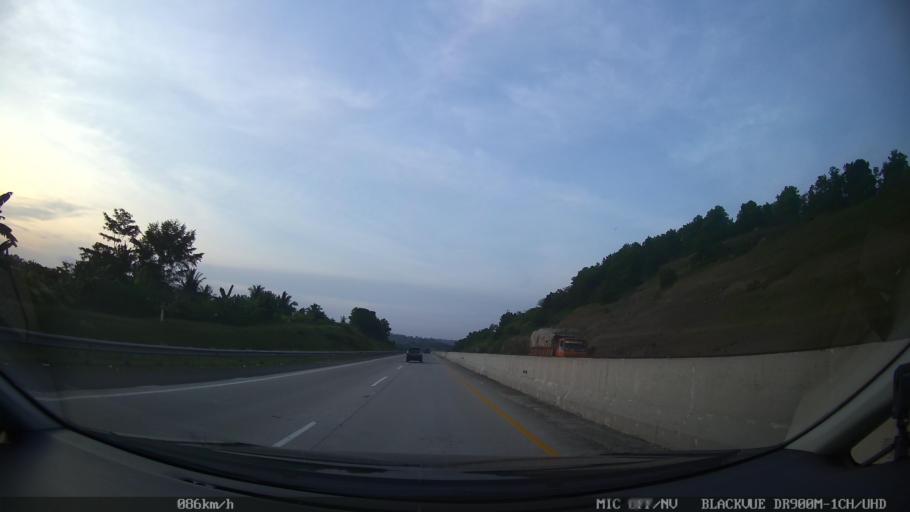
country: ID
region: Lampung
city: Penengahan
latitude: -5.8538
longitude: 105.7289
